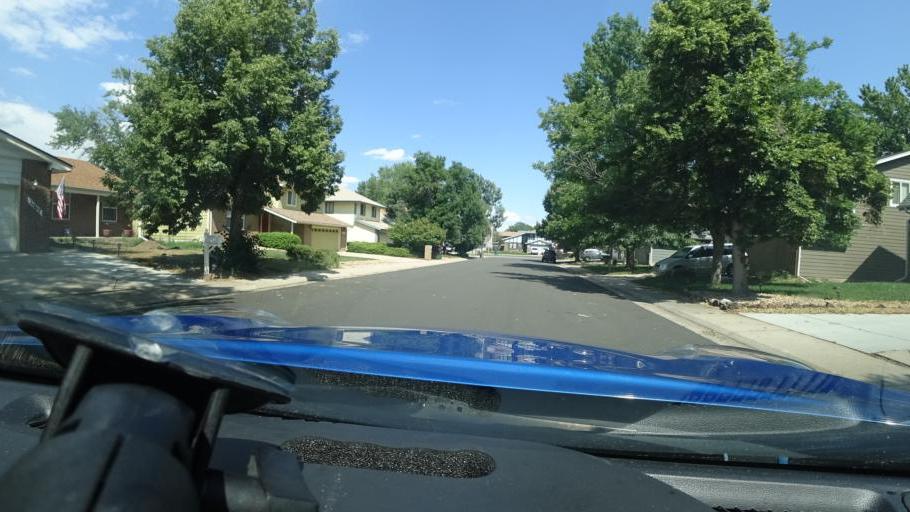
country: US
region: Colorado
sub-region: Adams County
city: Aurora
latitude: 39.6809
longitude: -104.8511
